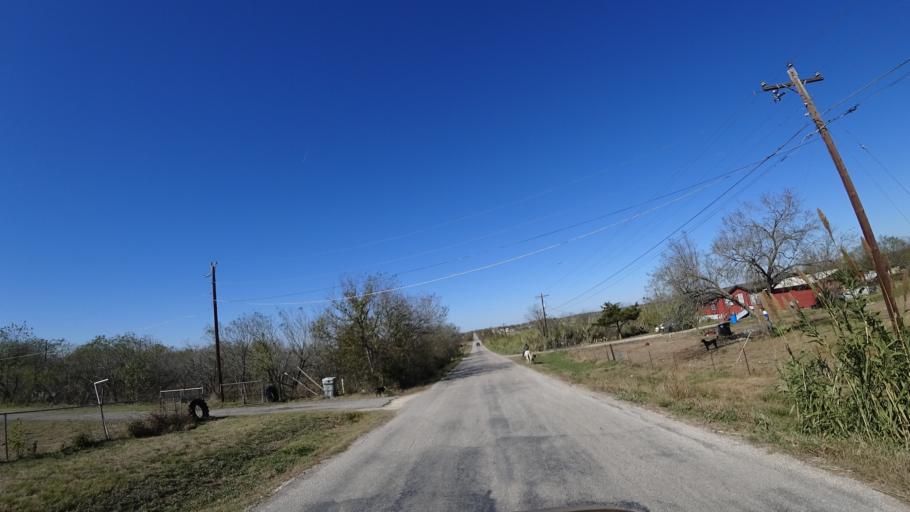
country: US
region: Texas
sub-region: Travis County
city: Garfield
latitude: 30.1135
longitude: -97.5868
